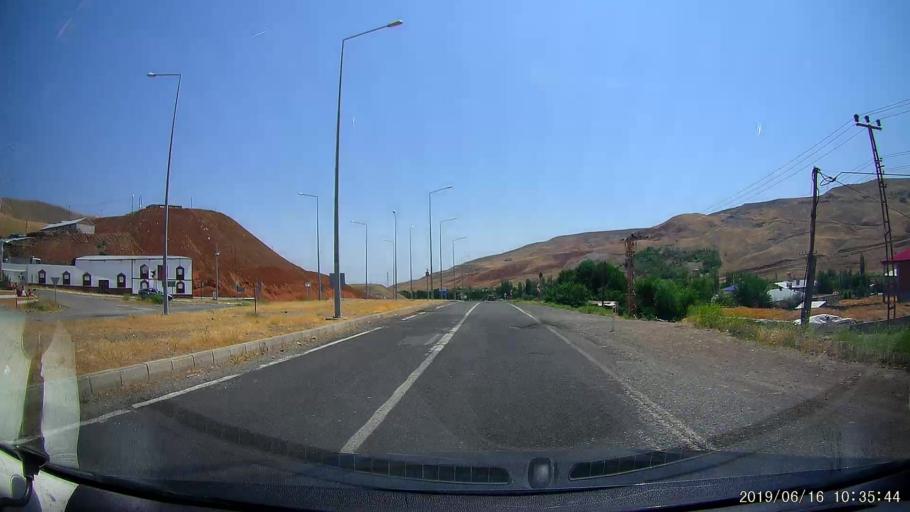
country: TR
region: Igdir
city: Tuzluca
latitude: 40.0359
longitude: 43.6738
